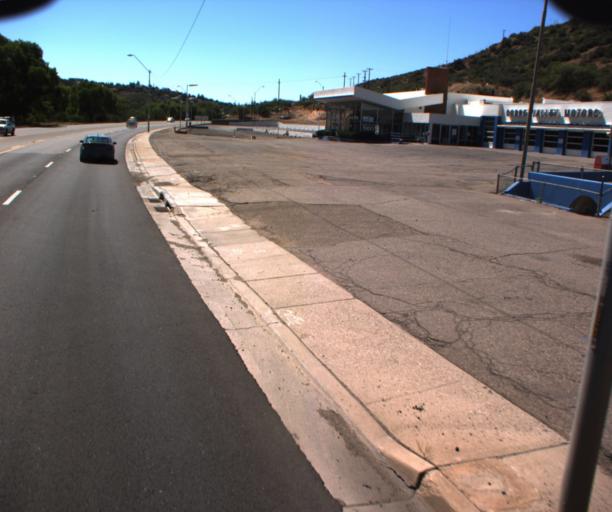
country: US
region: Arizona
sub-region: Gila County
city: Central Heights-Midland City
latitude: 33.4139
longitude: -110.7974
